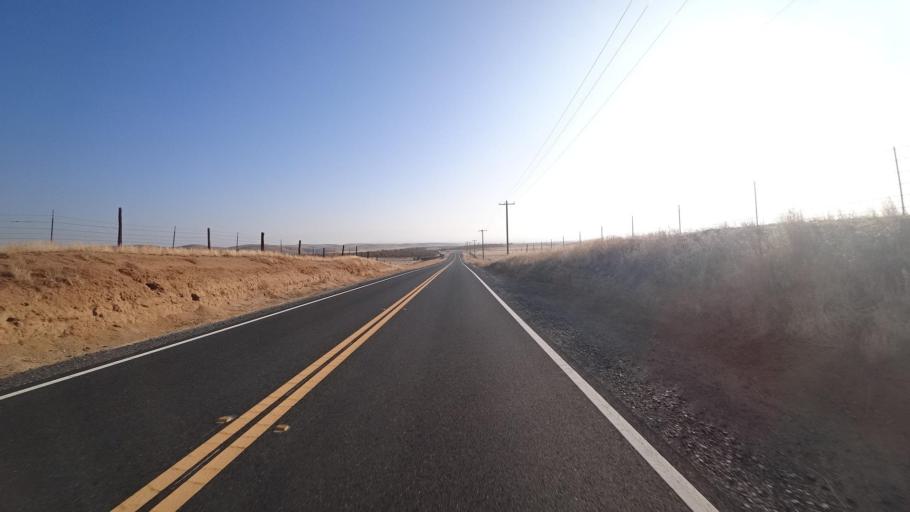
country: US
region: California
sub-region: Tulare County
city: Richgrove
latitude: 35.7621
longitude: -119.0392
